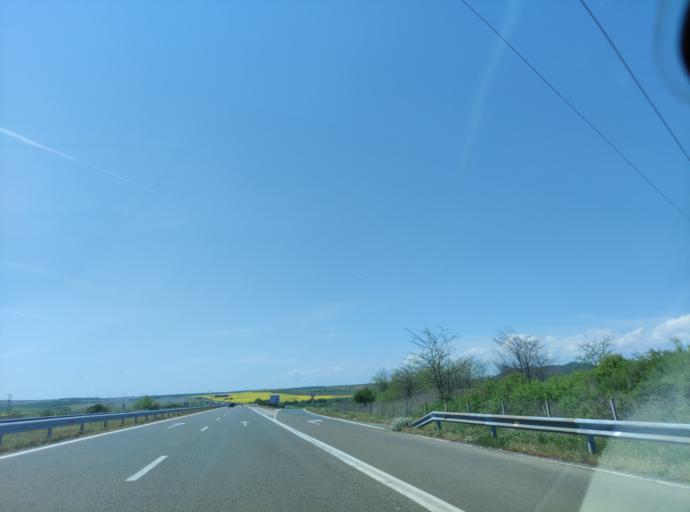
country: BG
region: Burgas
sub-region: Obshtina Kameno
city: Kameno
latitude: 42.6040
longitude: 27.3070
